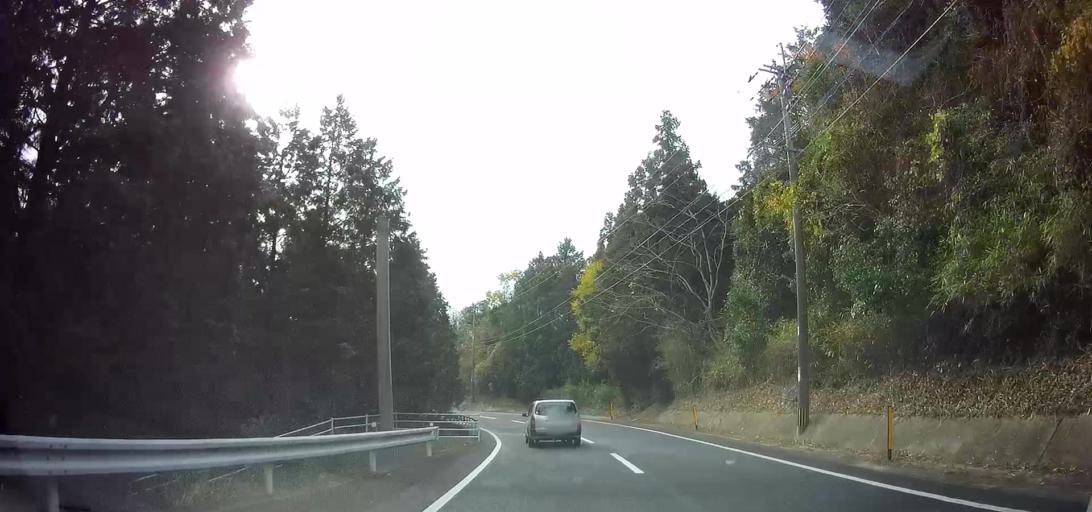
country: JP
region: Nagasaki
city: Shimabara
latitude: 32.6924
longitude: 130.2567
